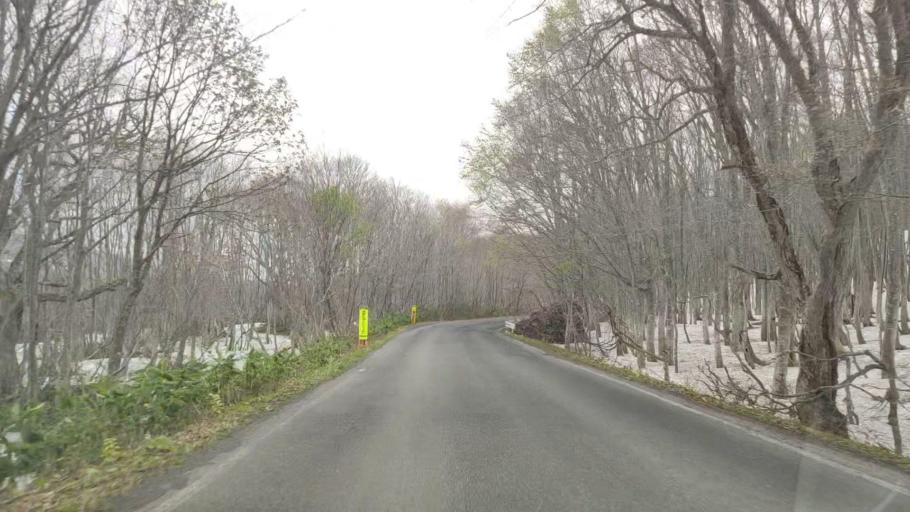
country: JP
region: Aomori
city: Aomori Shi
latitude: 40.6827
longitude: 140.9288
